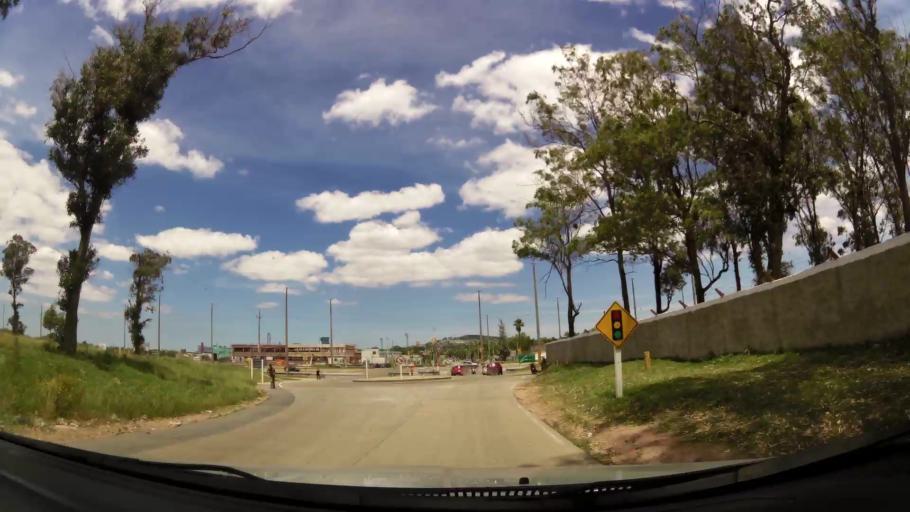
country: UY
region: Montevideo
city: Montevideo
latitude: -34.8634
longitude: -56.2523
